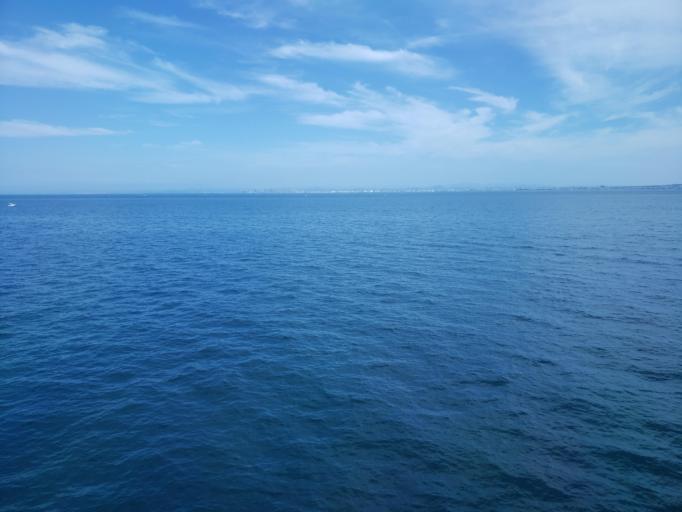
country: JP
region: Hyogo
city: Akashi
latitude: 34.5958
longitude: 134.9035
